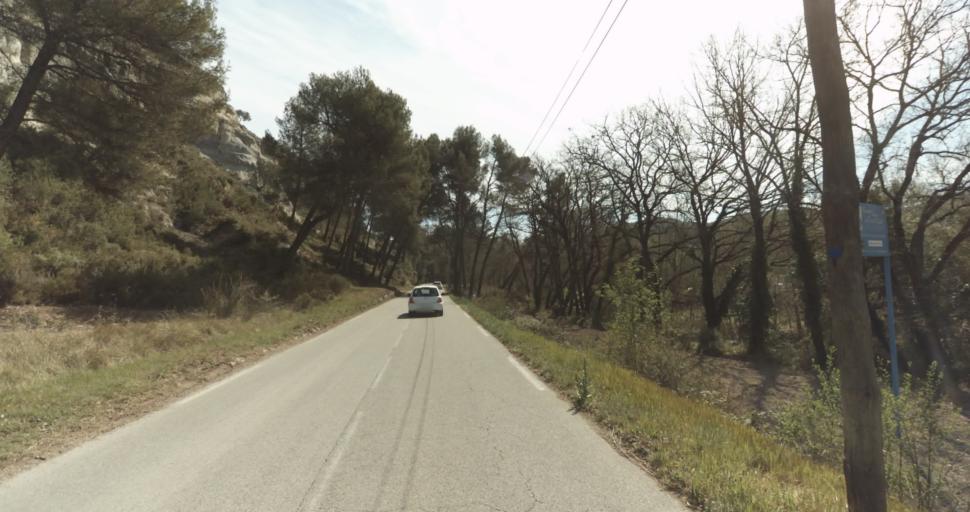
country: FR
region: Provence-Alpes-Cote d'Azur
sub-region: Departement des Bouches-du-Rhone
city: Ventabren
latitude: 43.5252
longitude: 5.2931
